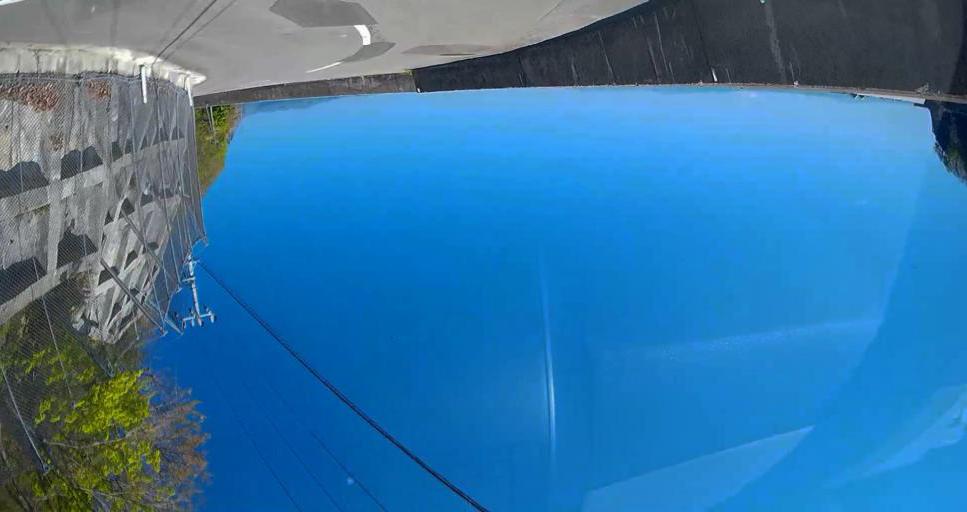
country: JP
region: Aomori
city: Aomori Shi
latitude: 41.1388
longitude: 140.7788
